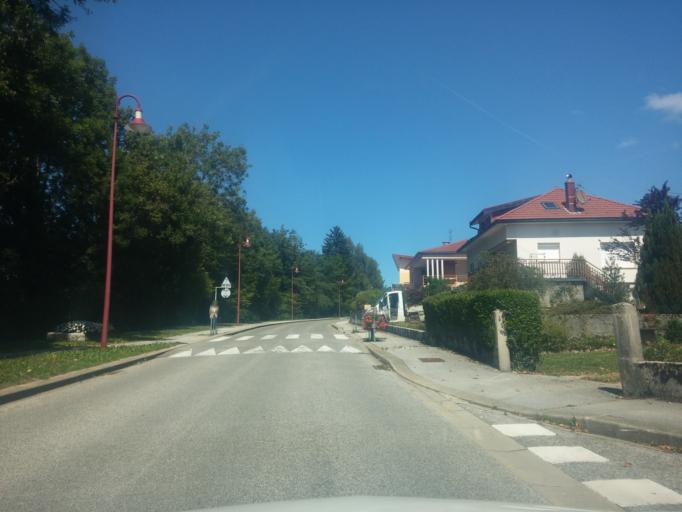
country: FR
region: Franche-Comte
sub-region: Departement du Jura
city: Saint-Lupicin
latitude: 46.4076
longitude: 5.7947
